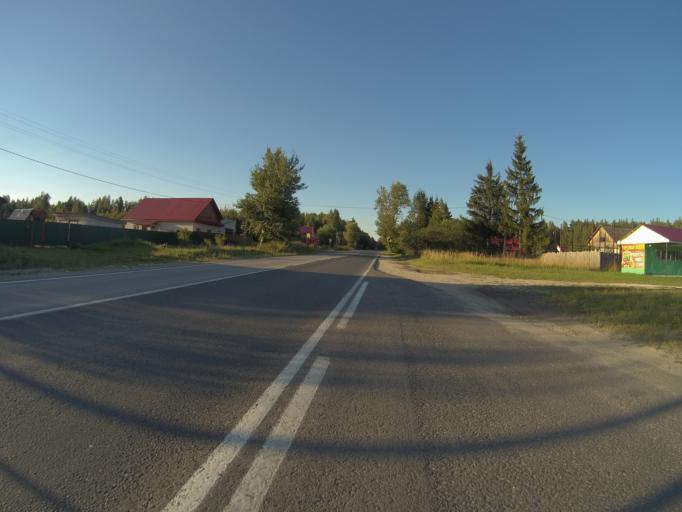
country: RU
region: Vladimir
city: Anopino
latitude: 55.6891
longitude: 40.7460
